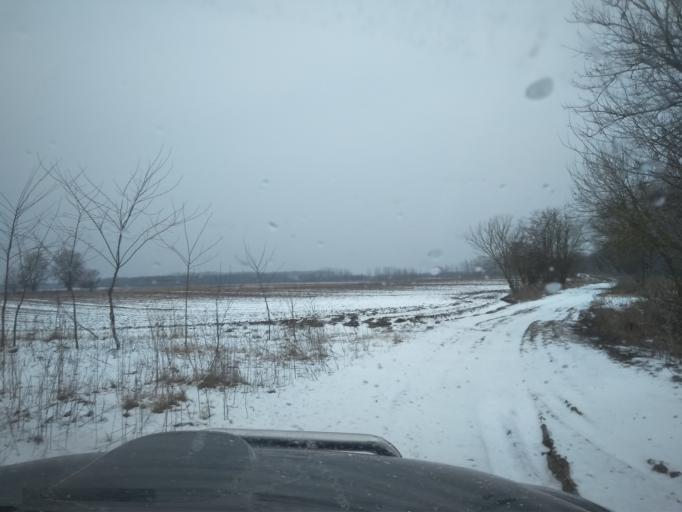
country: HU
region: Szabolcs-Szatmar-Bereg
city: Apagy
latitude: 47.9753
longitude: 21.9154
